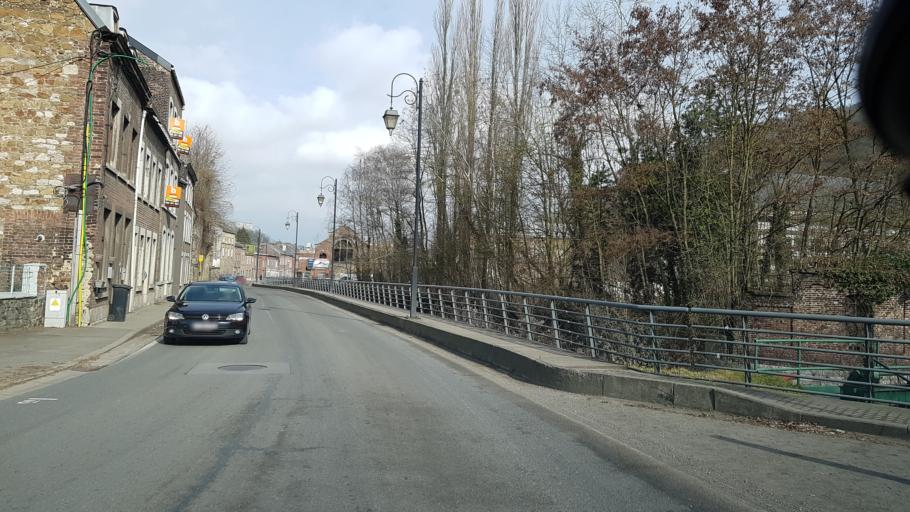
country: BE
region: Wallonia
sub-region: Province de Liege
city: Huy
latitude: 50.5094
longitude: 5.2394
